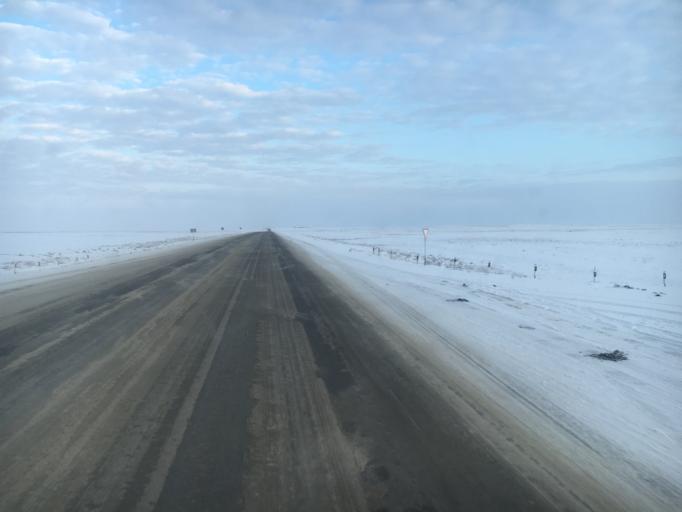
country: KZ
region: Qyzylorda
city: Sekseuil
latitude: 47.4148
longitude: 61.5384
